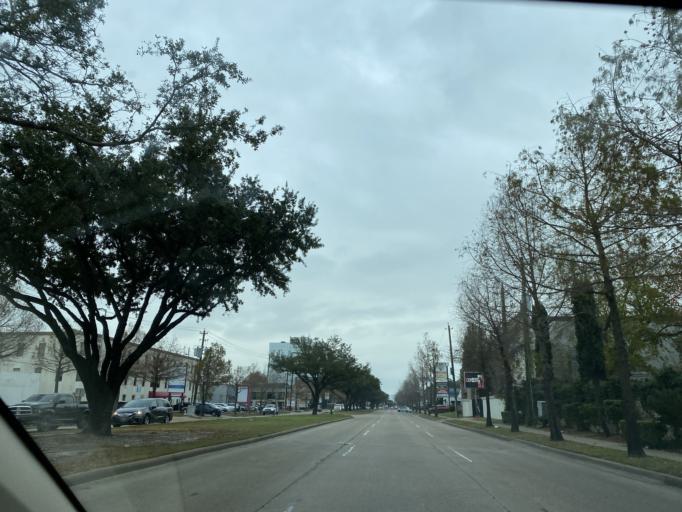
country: US
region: Texas
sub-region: Harris County
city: Piney Point Village
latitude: 29.7317
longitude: -95.4948
